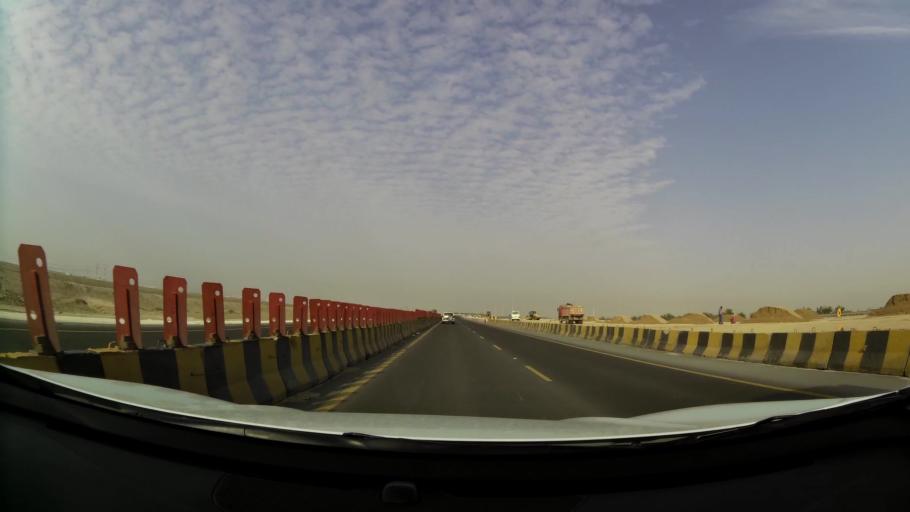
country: AE
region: Abu Dhabi
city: Abu Dhabi
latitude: 24.2388
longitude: 54.4640
